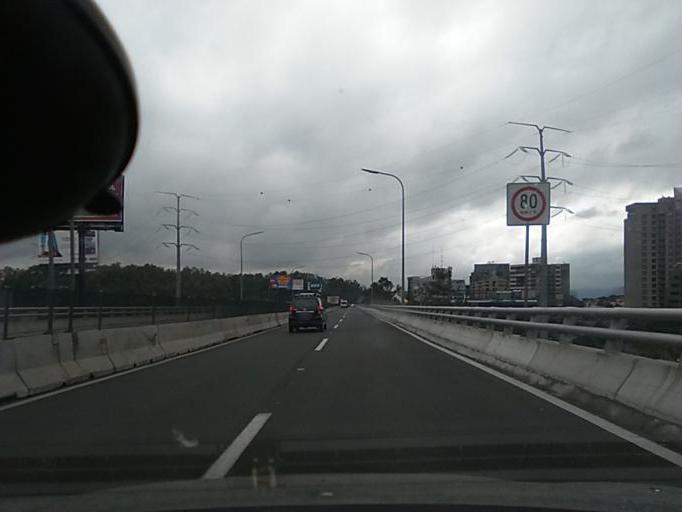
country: MX
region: Mexico City
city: Magdalena Contreras
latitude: 19.3059
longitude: -99.2075
